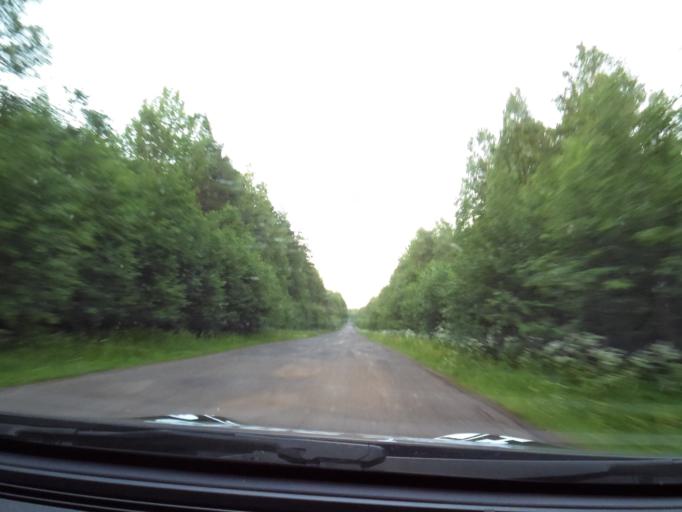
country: RU
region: Leningrad
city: Voznesen'ye
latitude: 60.8413
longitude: 35.6314
